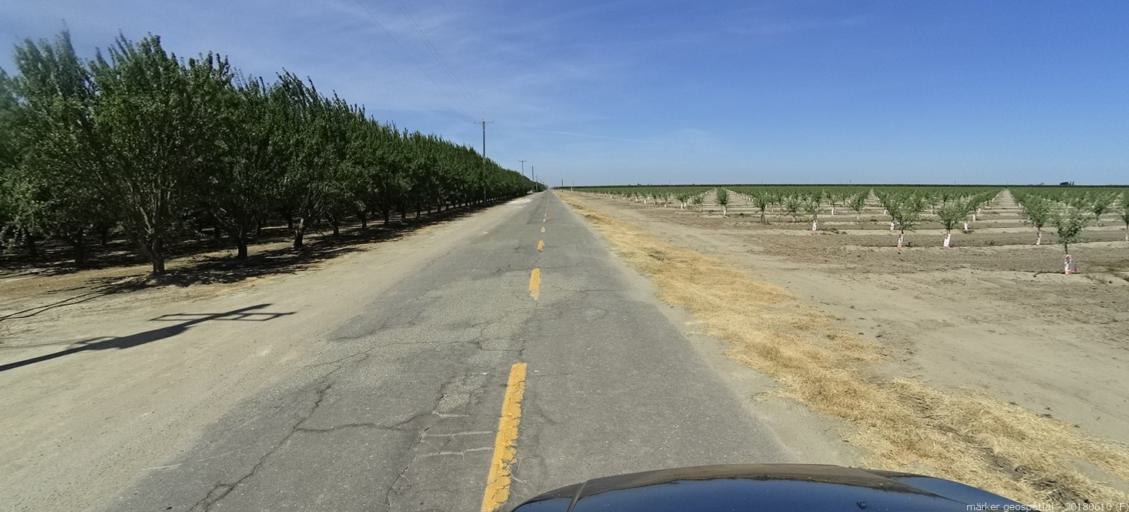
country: US
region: California
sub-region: Madera County
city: Chowchilla
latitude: 37.0399
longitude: -120.3481
